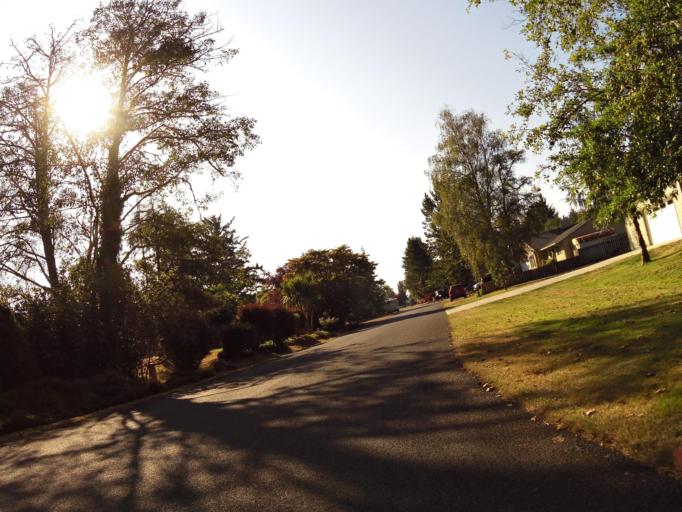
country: US
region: Oregon
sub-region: Clatsop County
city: Warrenton
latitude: 46.1387
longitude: -123.9354
